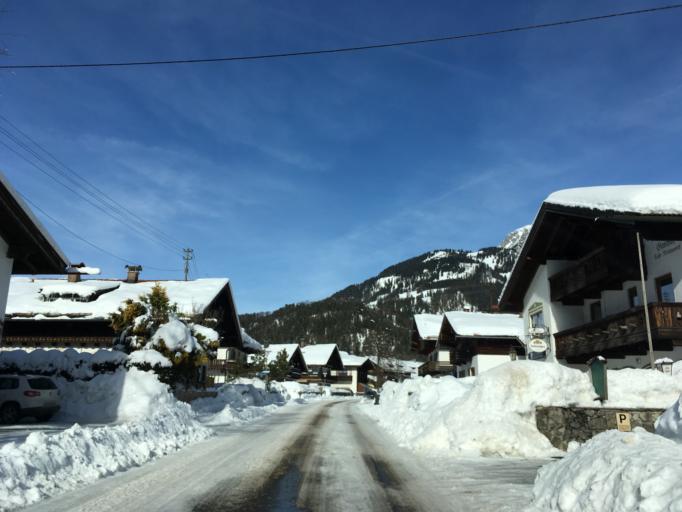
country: DE
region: Bavaria
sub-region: Upper Bavaria
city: Bayrischzell
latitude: 47.6720
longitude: 12.0145
